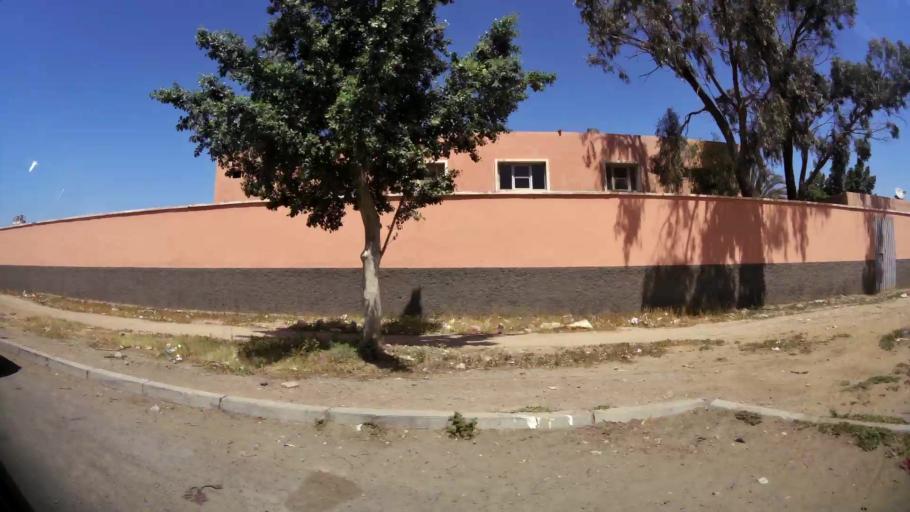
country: MA
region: Souss-Massa-Draa
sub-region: Inezgane-Ait Mellou
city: Inezgane
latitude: 30.3277
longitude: -9.4868
